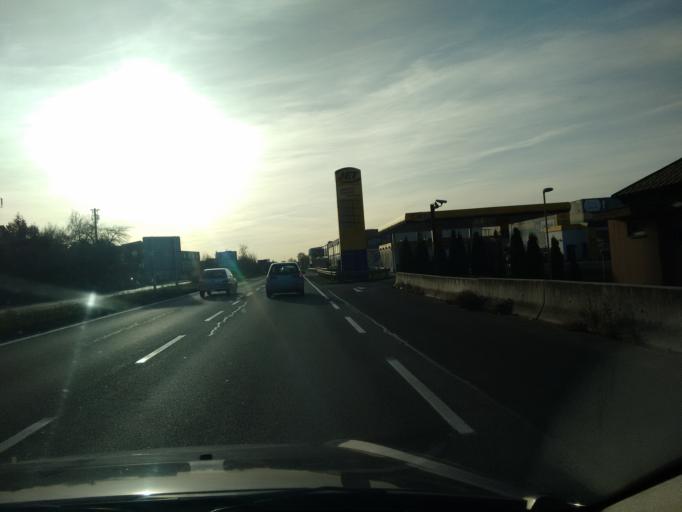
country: AT
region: Upper Austria
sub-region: Wels Stadt
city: Wels
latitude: 48.1796
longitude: 14.0631
